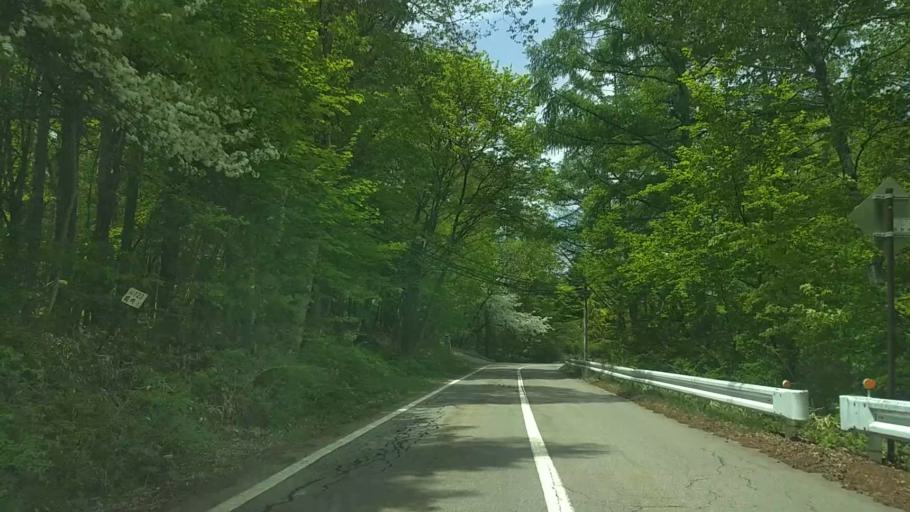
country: JP
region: Nagano
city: Saku
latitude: 36.1079
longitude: 138.4116
